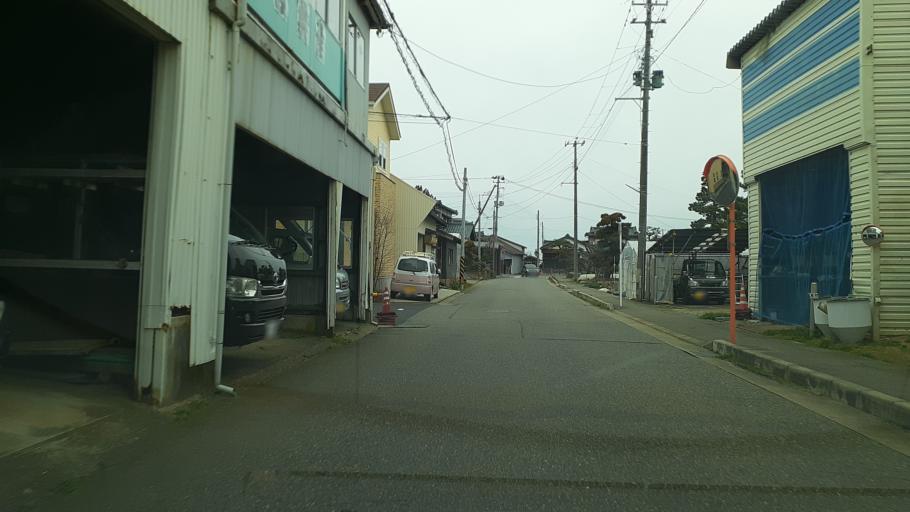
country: JP
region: Niigata
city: Niigata-shi
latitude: 37.8602
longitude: 139.0370
